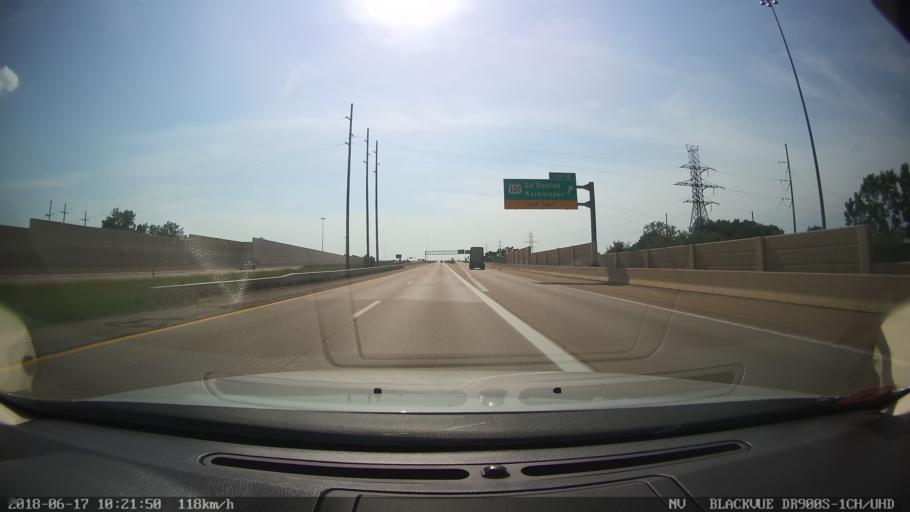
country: US
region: Michigan
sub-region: Kent County
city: Cutlerville
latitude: 42.8490
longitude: -85.6664
